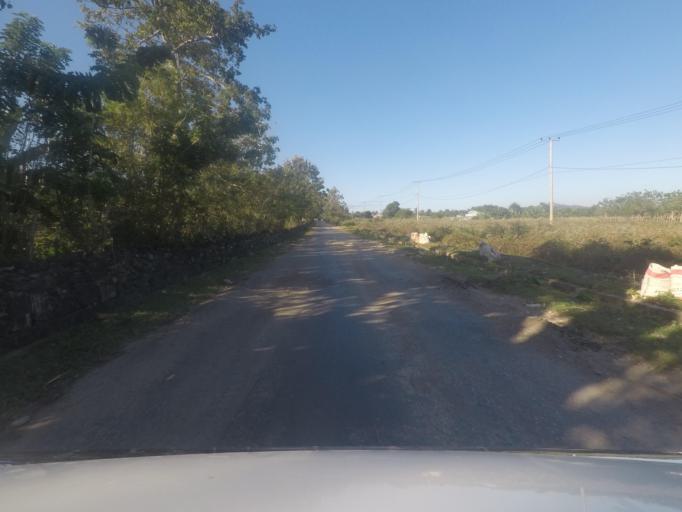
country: TL
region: Lautem
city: Lospalos
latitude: -8.4046
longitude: 127.1762
